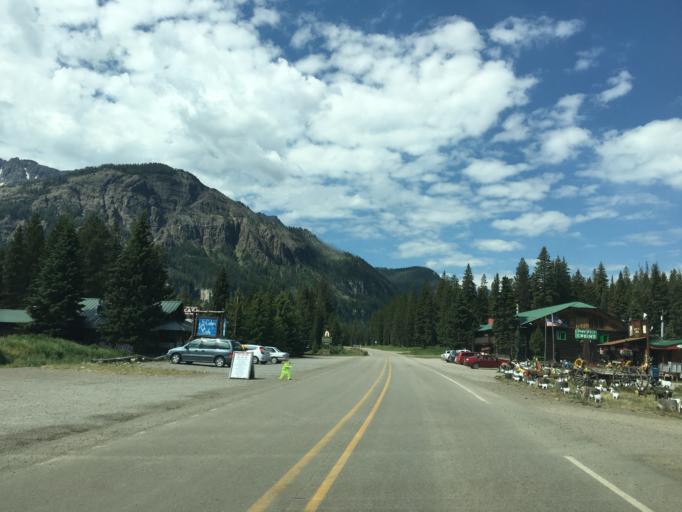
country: US
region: Montana
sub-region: Stillwater County
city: Absarokee
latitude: 45.0070
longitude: -109.9897
